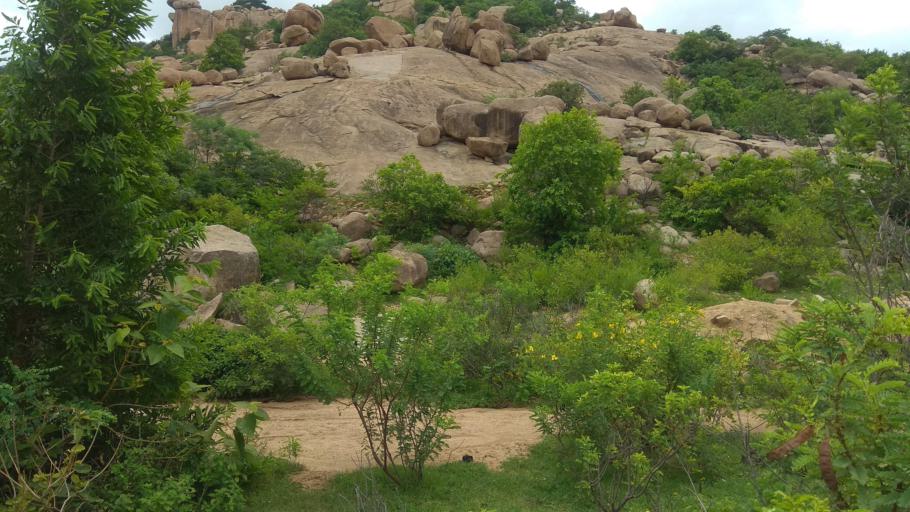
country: IN
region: Telangana
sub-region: Mahbubnagar
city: Farrukhnagar
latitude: 16.8898
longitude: 78.4955
